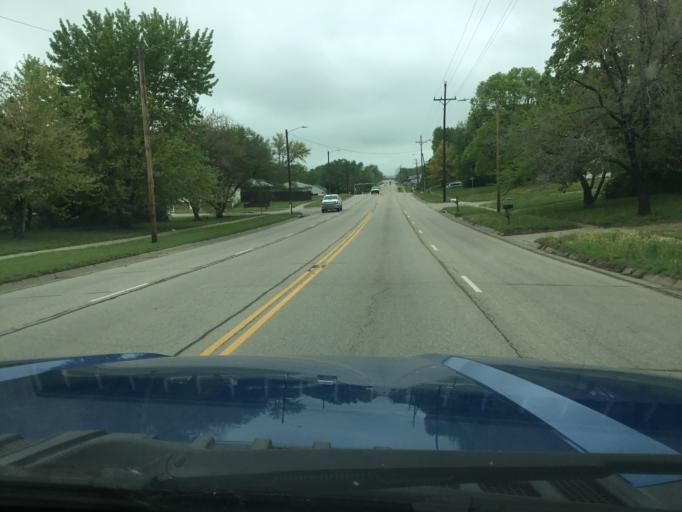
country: US
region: Kansas
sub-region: Shawnee County
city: Topeka
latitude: 39.0200
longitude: -95.6701
